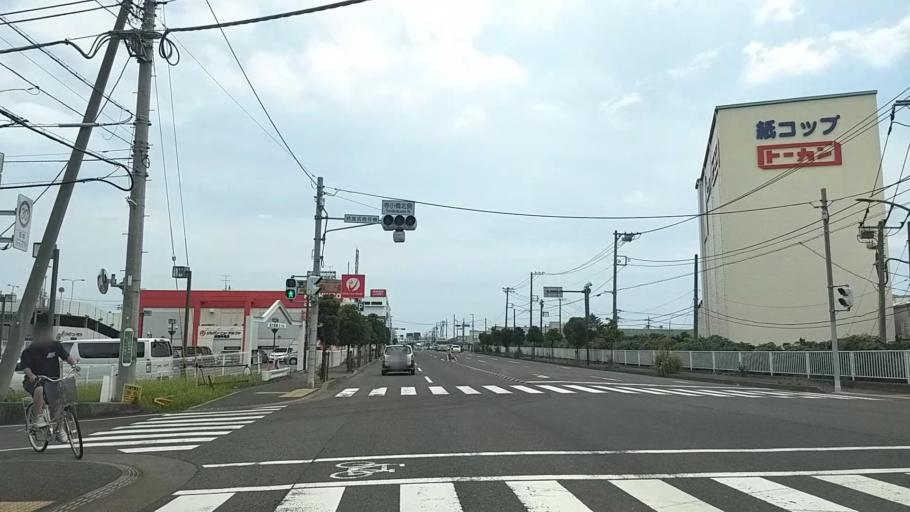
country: JP
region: Kanagawa
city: Minami-rinkan
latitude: 35.4504
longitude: 139.4193
